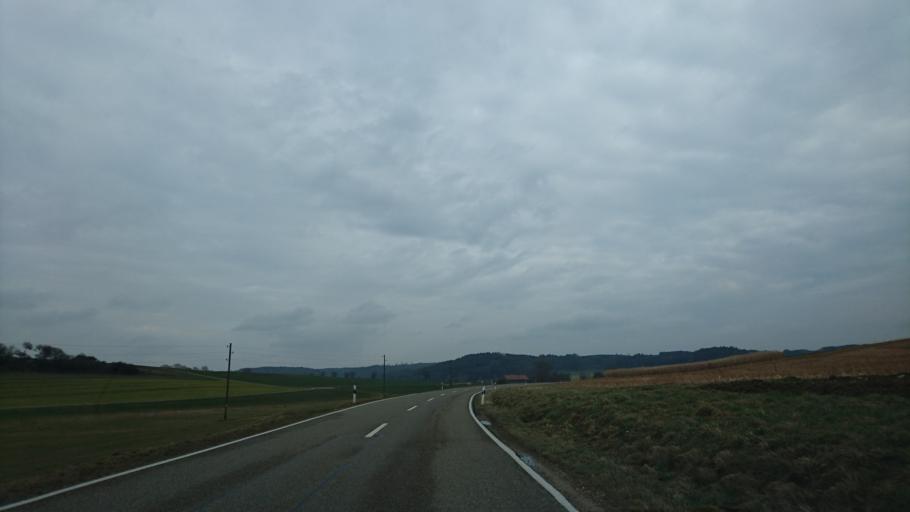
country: DE
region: Bavaria
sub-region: Swabia
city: Altenmunster
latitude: 48.4899
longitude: 10.5906
